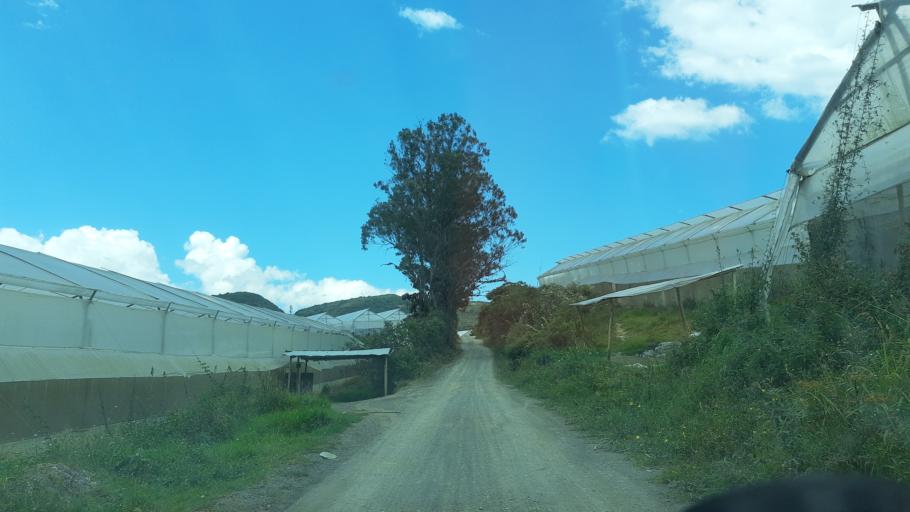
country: CO
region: Boyaca
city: Santa Sofia
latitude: 5.6888
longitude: -73.5695
